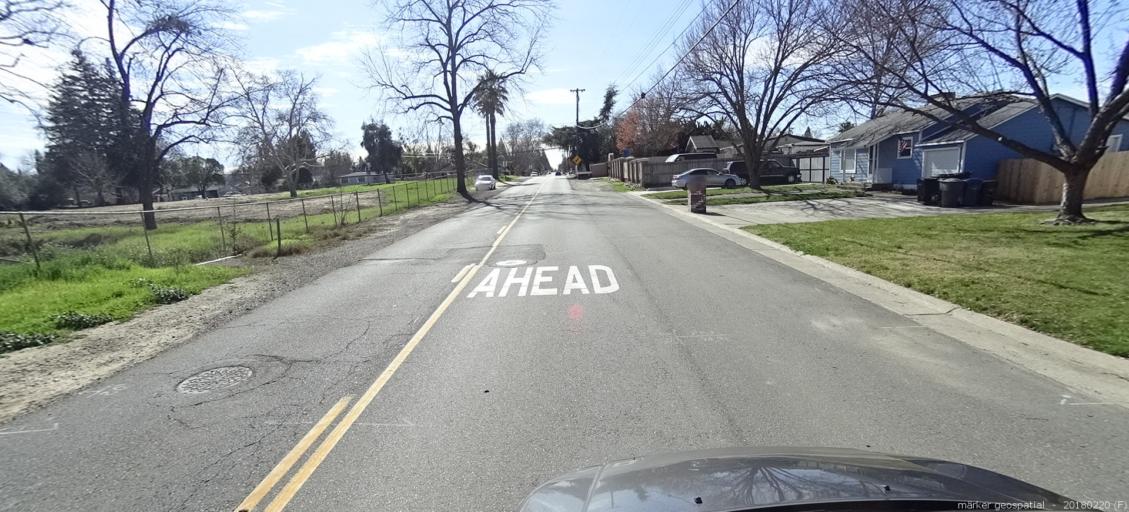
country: US
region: California
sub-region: Sacramento County
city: Orangevale
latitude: 38.6868
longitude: -121.2208
